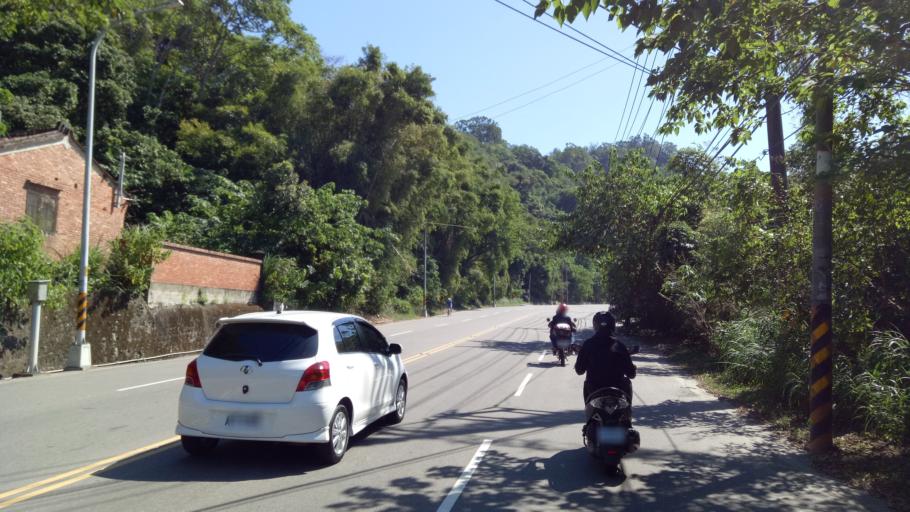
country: TW
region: Taiwan
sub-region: Hsinchu
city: Hsinchu
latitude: 24.6809
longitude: 120.9650
